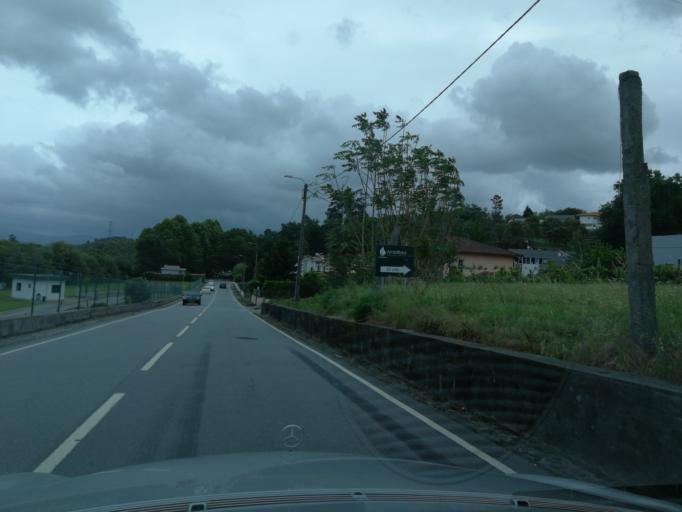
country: PT
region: Braga
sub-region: Braga
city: Adaufe
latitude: 41.6040
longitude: -8.4259
